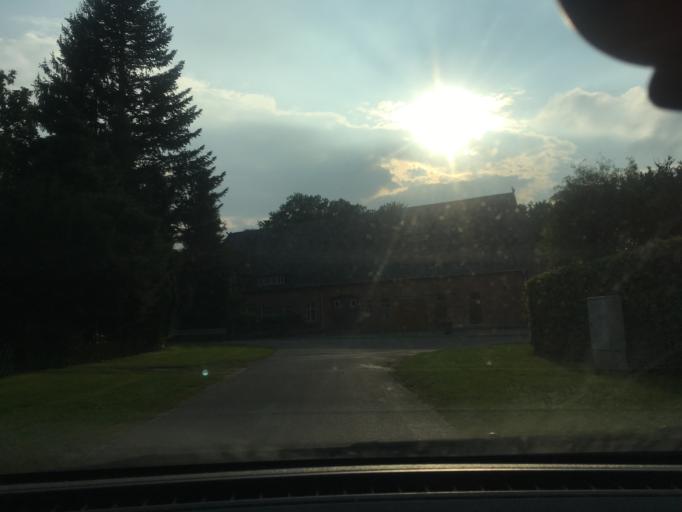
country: DE
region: Lower Saxony
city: Reinstorf
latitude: 53.2016
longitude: 10.5807
